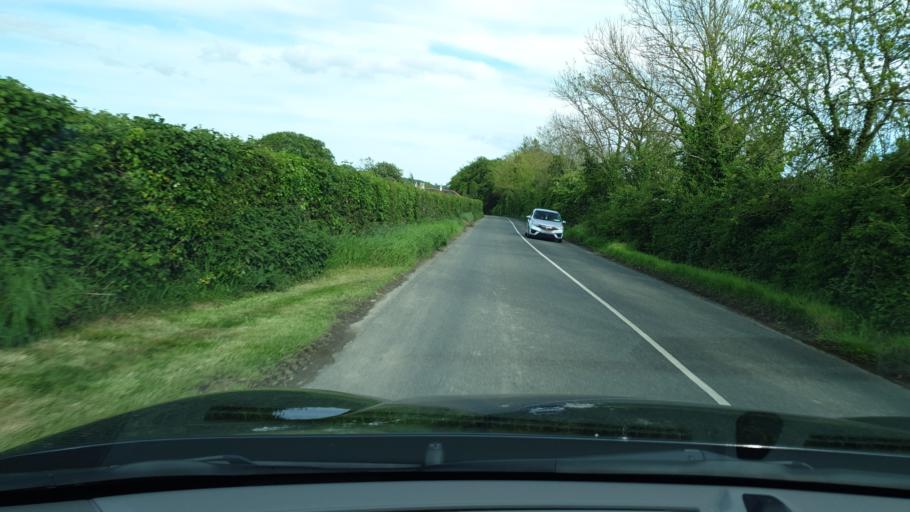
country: IE
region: Leinster
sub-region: An Mhi
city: Ashbourne
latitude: 53.5621
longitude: -6.3437
